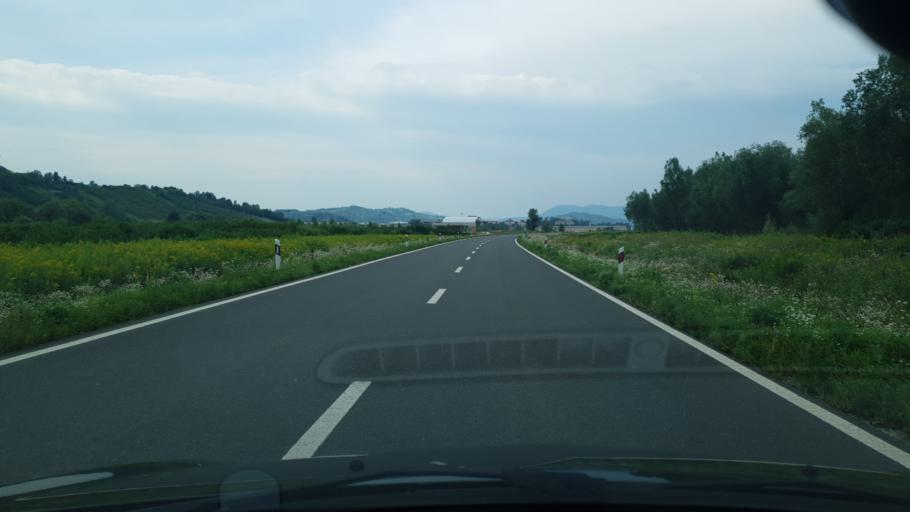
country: HR
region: Krapinsko-Zagorska
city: Zabok
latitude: 46.0629
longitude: 15.9145
